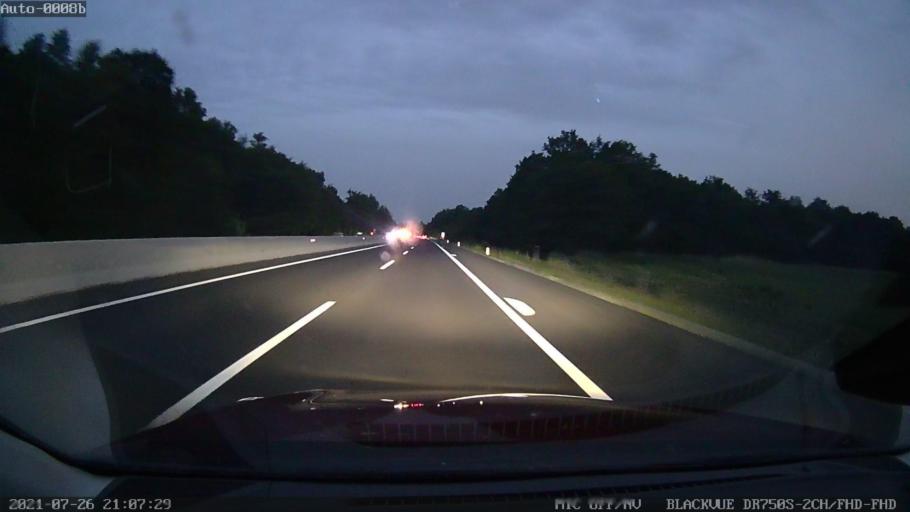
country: AT
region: Styria
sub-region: Politischer Bezirk Leibnitz
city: Gabersdorf
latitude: 46.7892
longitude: 15.5738
